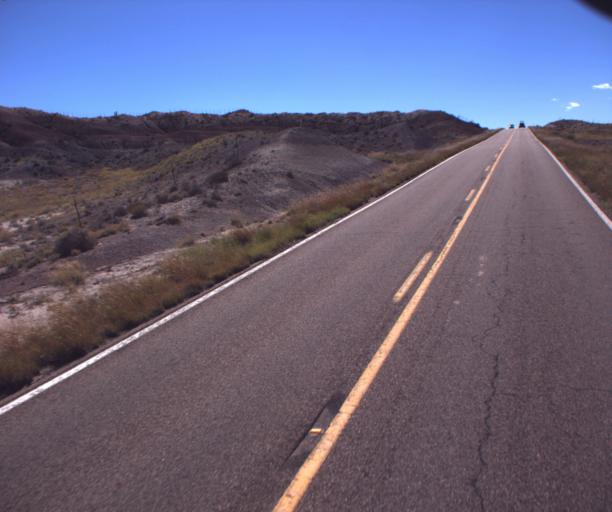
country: US
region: Arizona
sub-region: Apache County
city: Saint Johns
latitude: 34.6602
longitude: -109.2940
